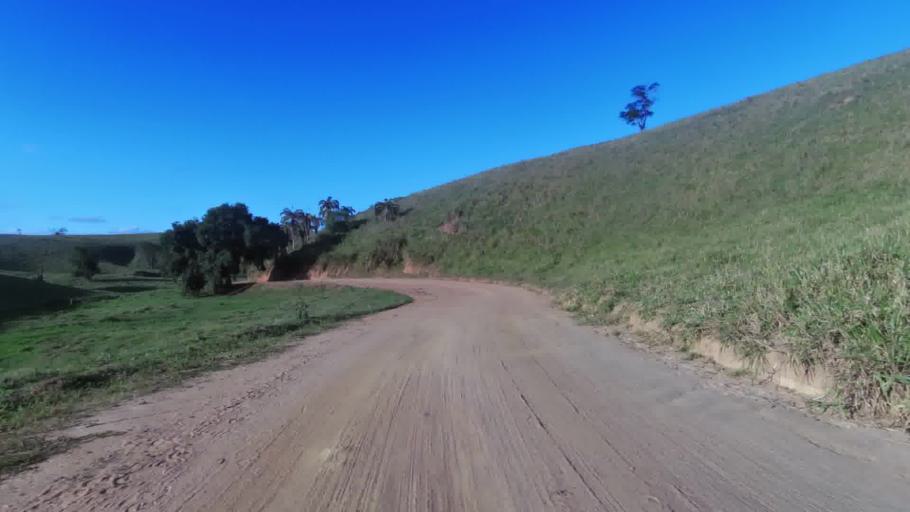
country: BR
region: Espirito Santo
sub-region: Marataizes
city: Marataizes
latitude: -21.1451
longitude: -41.0282
